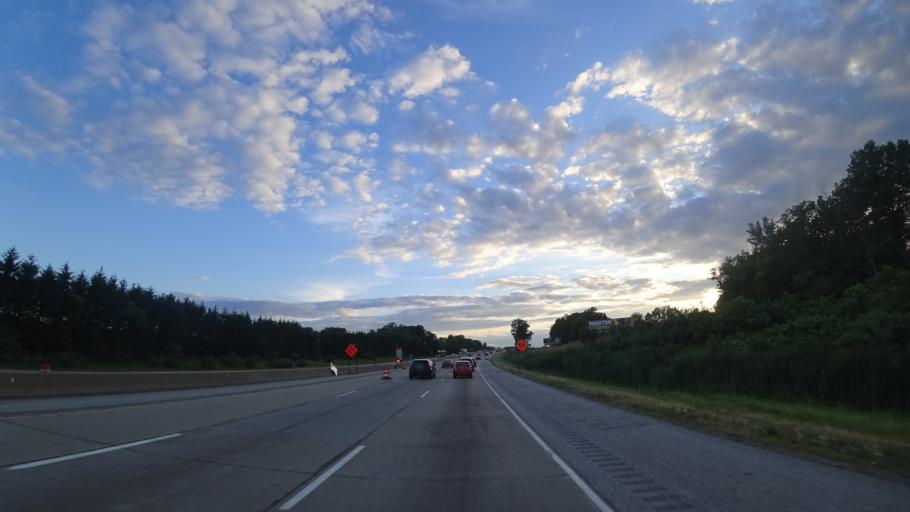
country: US
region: Indiana
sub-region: Porter County
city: Chesterton
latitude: 41.6262
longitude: -87.0255
